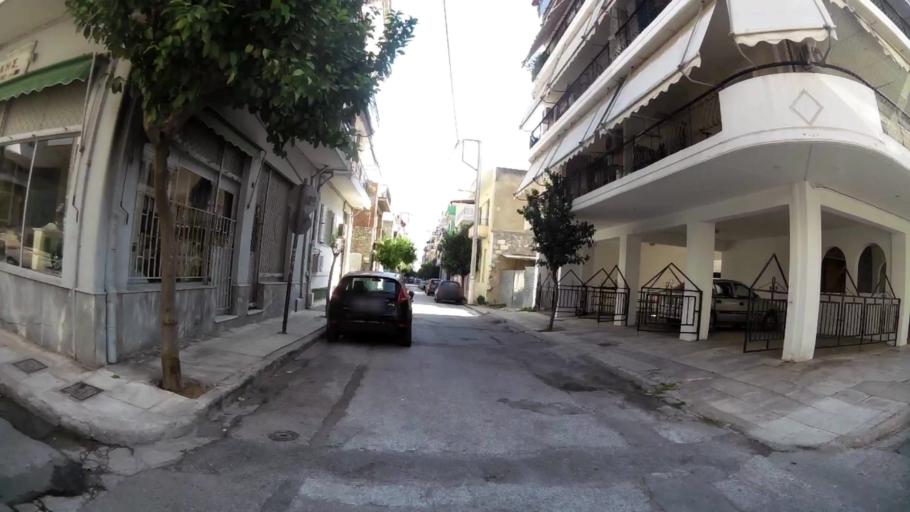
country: GR
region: Attica
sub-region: Nomos Piraios
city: Drapetsona
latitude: 37.9548
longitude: 23.6272
